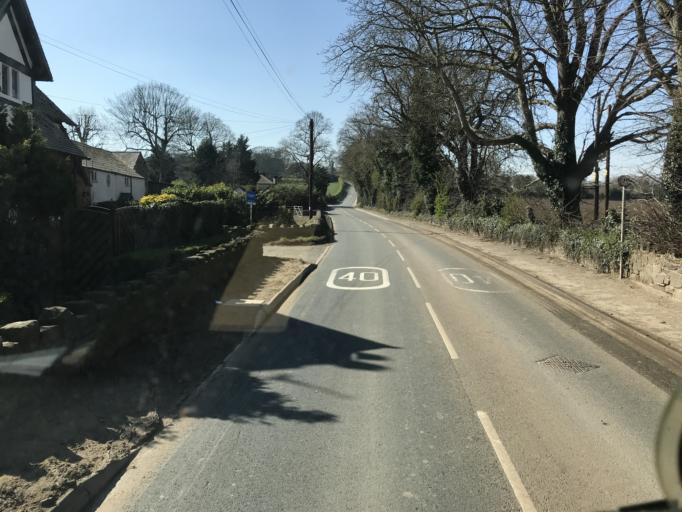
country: GB
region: Wales
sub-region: Wrexham
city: Gresford
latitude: 53.1059
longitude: -2.9678
